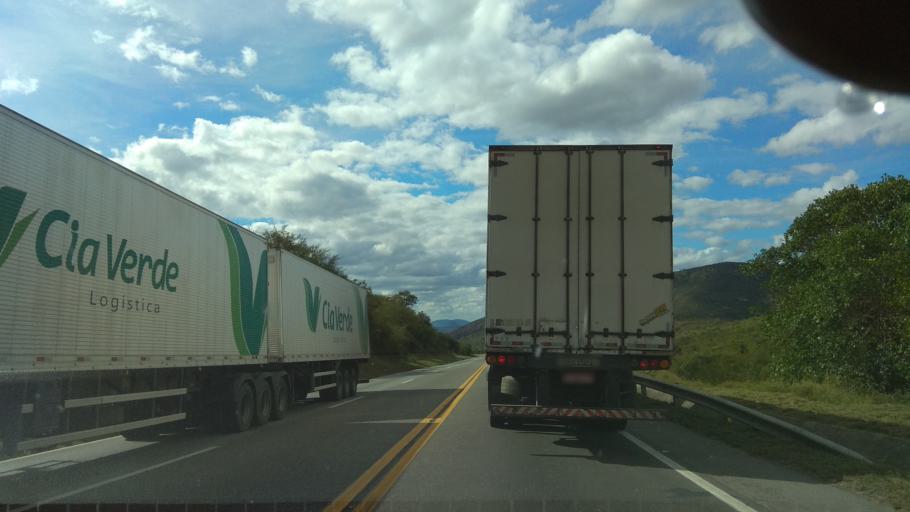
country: BR
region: Bahia
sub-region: Amargosa
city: Amargosa
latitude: -12.8936
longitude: -39.8599
